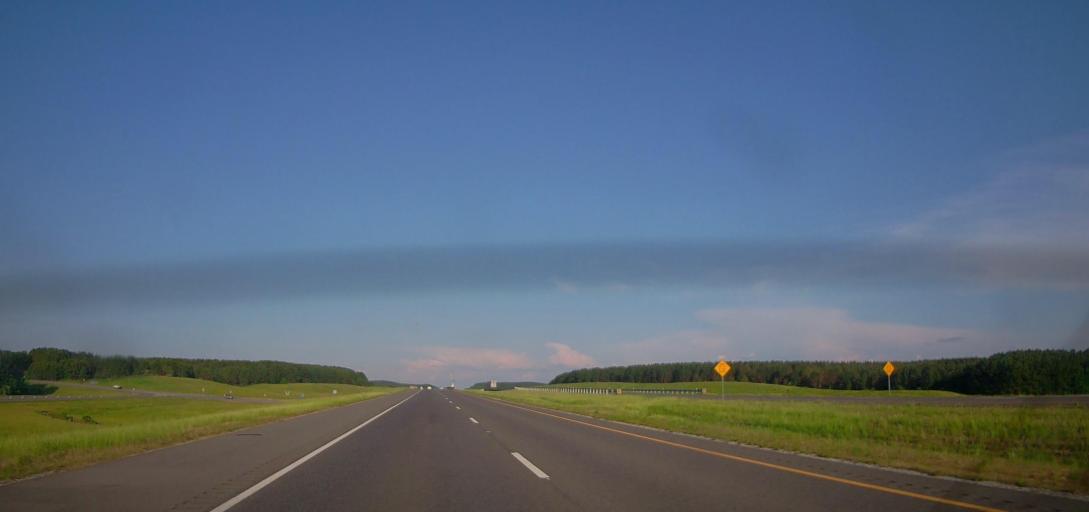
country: US
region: Alabama
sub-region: Walker County
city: Carbon Hill
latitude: 33.9525
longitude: -87.6184
